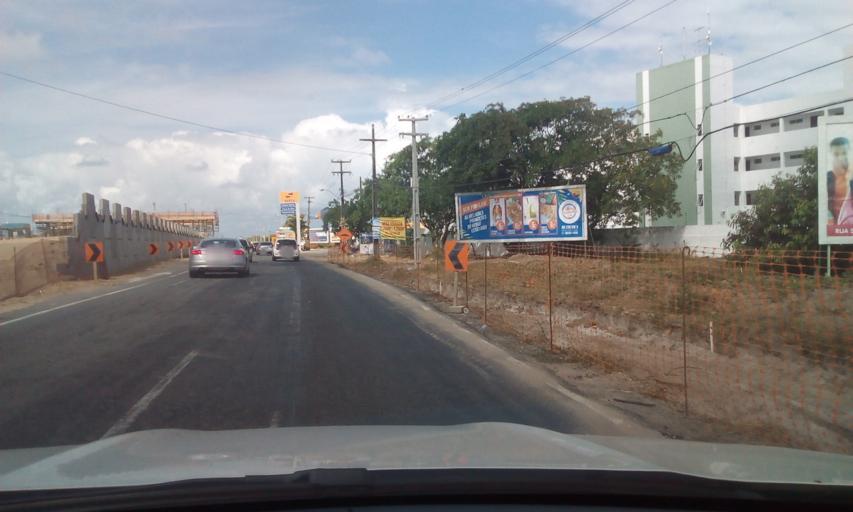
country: BR
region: Paraiba
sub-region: Cabedelo
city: Cabedelo
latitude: -7.0220
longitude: -34.8364
